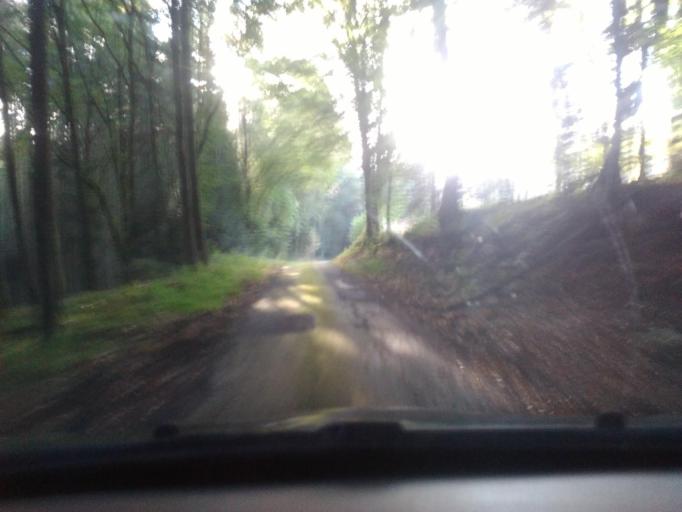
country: FR
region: Lorraine
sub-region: Departement des Vosges
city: Senones
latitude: 48.3936
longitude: 7.0635
